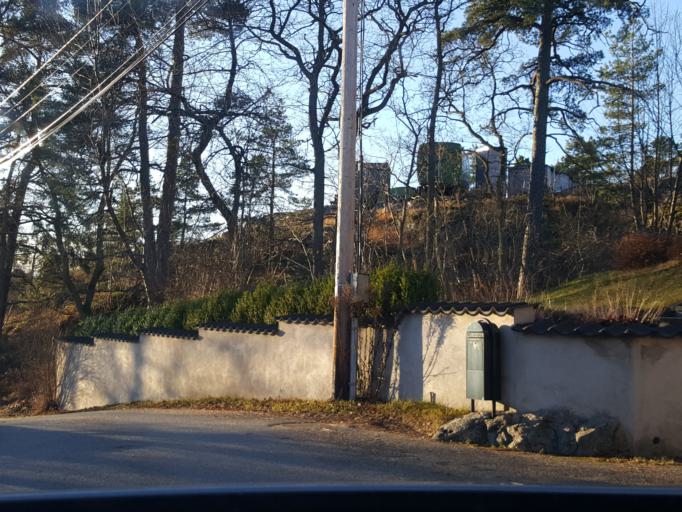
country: SE
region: Stockholm
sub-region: Lidingo
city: Brevik
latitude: 59.3177
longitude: 18.2191
